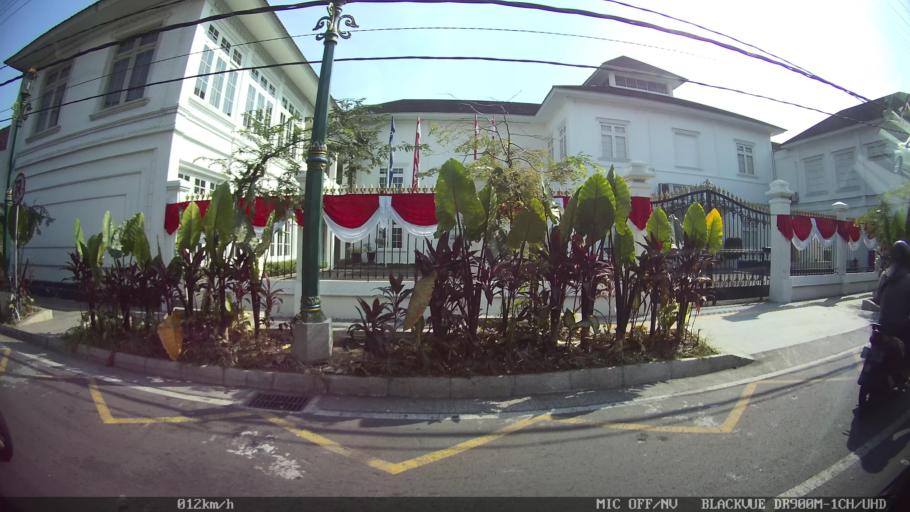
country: ID
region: Daerah Istimewa Yogyakarta
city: Yogyakarta
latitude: -7.8012
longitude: 110.3635
